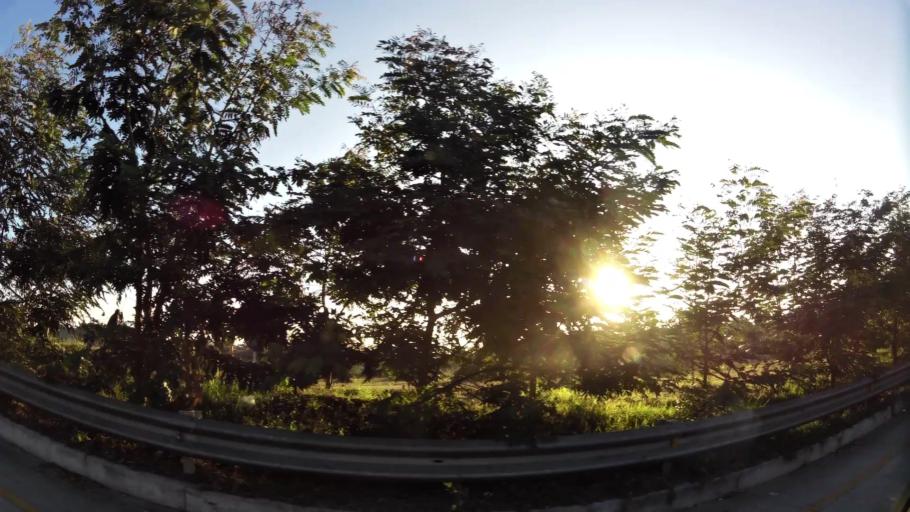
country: SV
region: La Libertad
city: Santa Tecla
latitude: 13.6831
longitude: -89.2639
